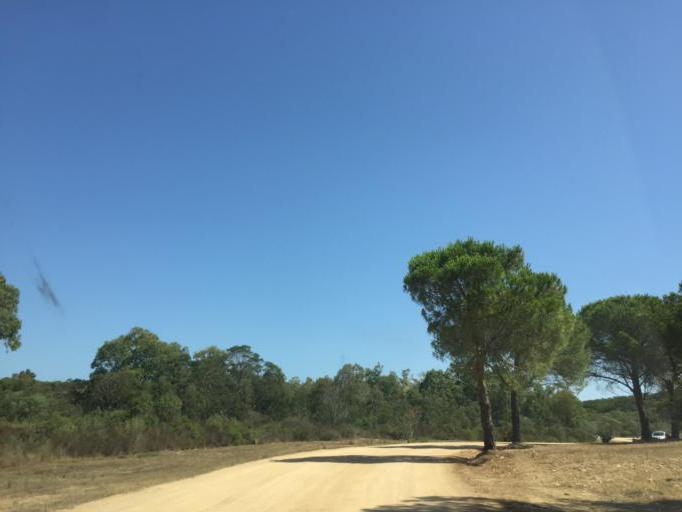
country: IT
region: Sardinia
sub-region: Provincia di Olbia-Tempio
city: San Teodoro
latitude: 40.8354
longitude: 9.6804
